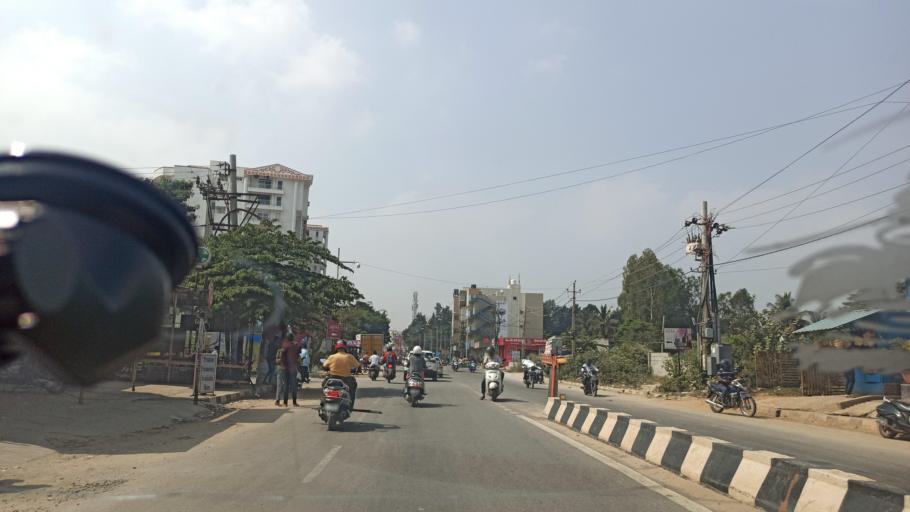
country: IN
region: Karnataka
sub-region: Bangalore Urban
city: Yelahanka
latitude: 13.1045
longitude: 77.6113
